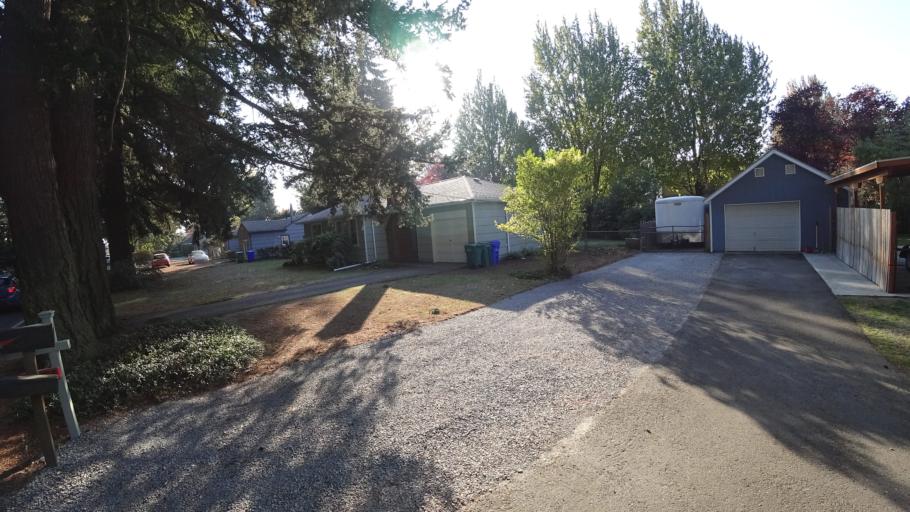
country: US
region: Oregon
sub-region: Multnomah County
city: Fairview
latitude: 45.5217
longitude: -122.4553
